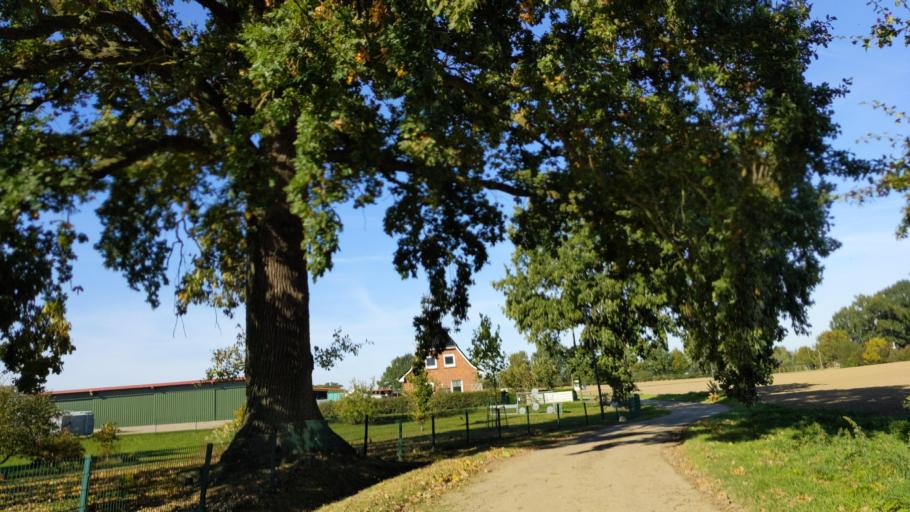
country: DE
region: Schleswig-Holstein
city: Ahrensbok
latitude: 54.0118
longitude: 10.6177
